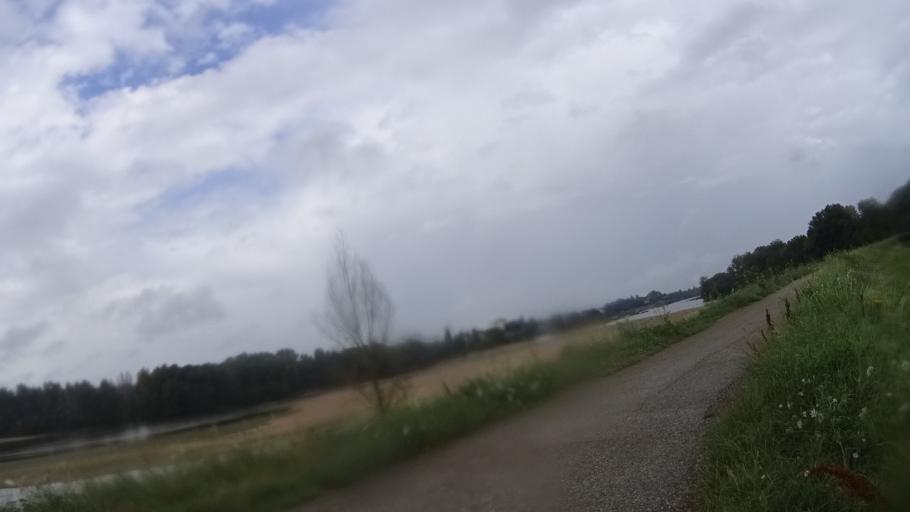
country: FR
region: Centre
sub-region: Departement du Loiret
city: Saint-Jean-le-Blanc
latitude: 47.8950
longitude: 1.9226
